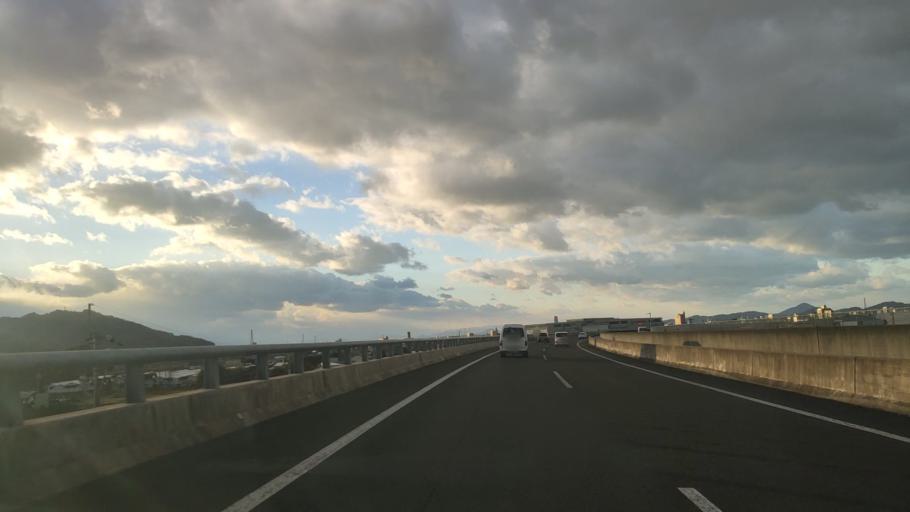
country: JP
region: Ehime
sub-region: Shikoku-chuo Shi
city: Matsuyama
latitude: 33.7885
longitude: 132.8093
